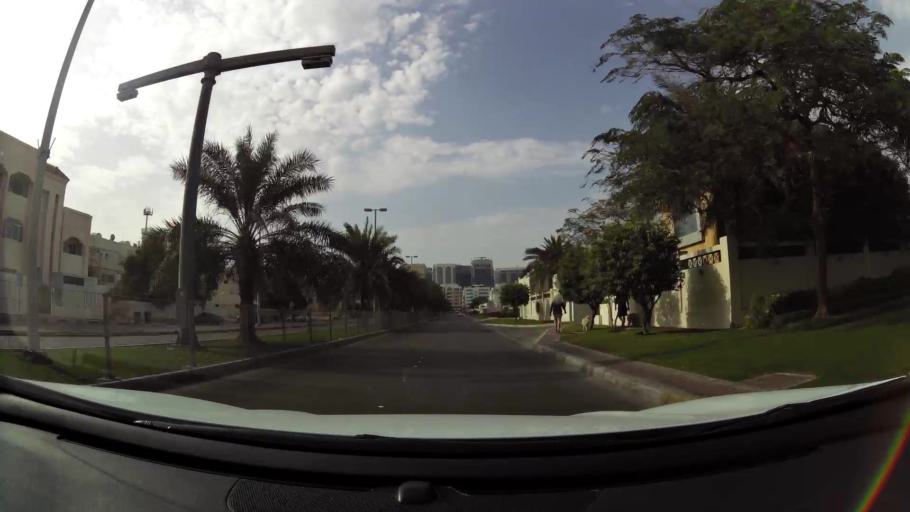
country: AE
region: Abu Dhabi
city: Abu Dhabi
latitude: 24.4670
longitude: 54.3509
